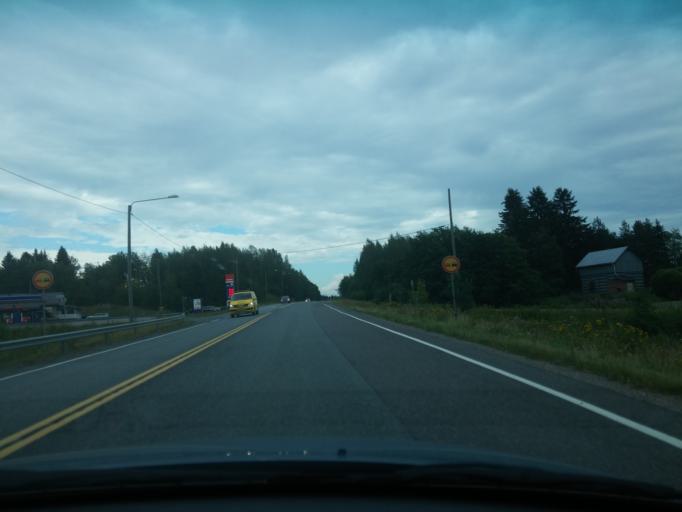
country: FI
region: Haeme
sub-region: Haemeenlinna
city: Tervakoski
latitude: 60.7383
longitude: 24.5795
